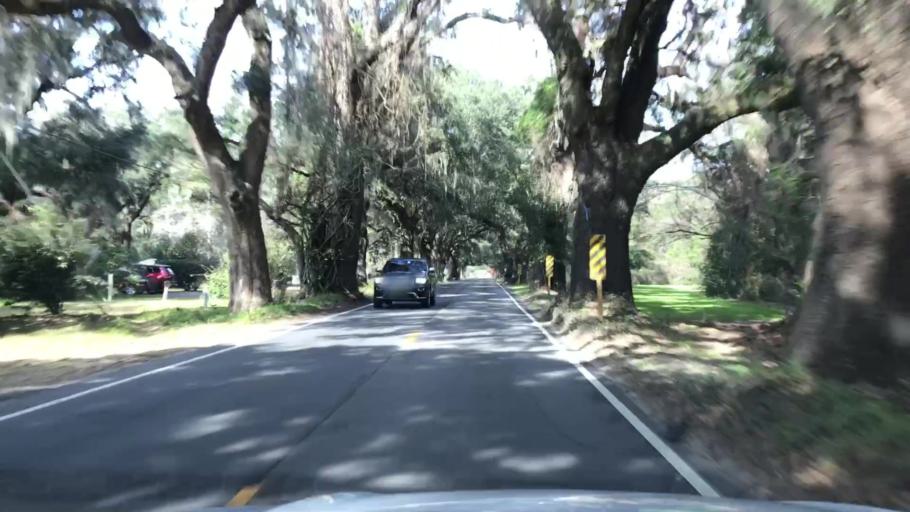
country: US
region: South Carolina
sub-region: Charleston County
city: Shell Point
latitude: 32.7375
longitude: -80.0338
